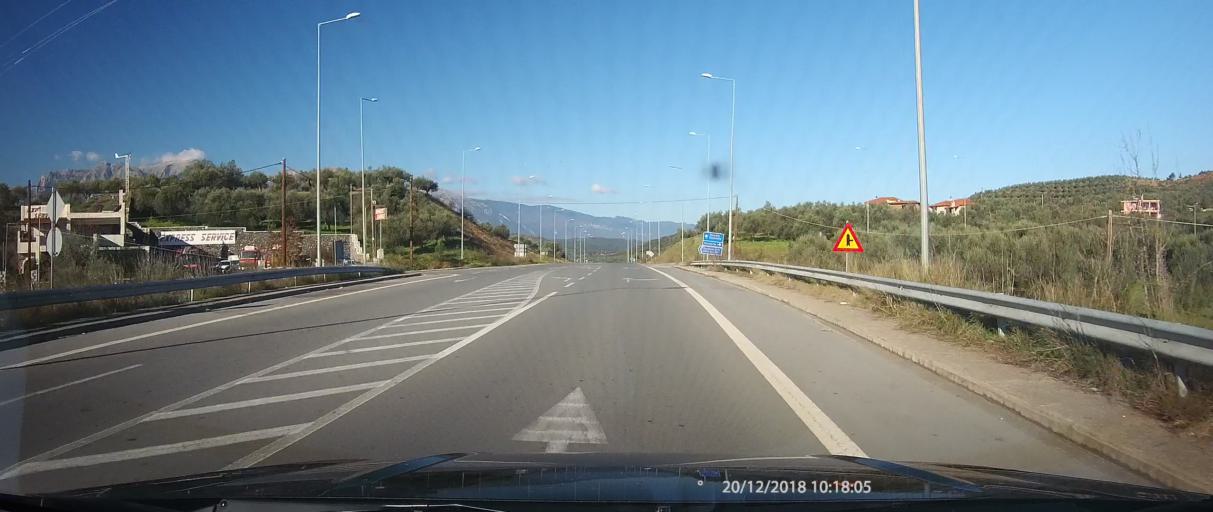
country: GR
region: Peloponnese
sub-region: Nomos Lakonias
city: Sparti
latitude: 37.1133
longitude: 22.4306
